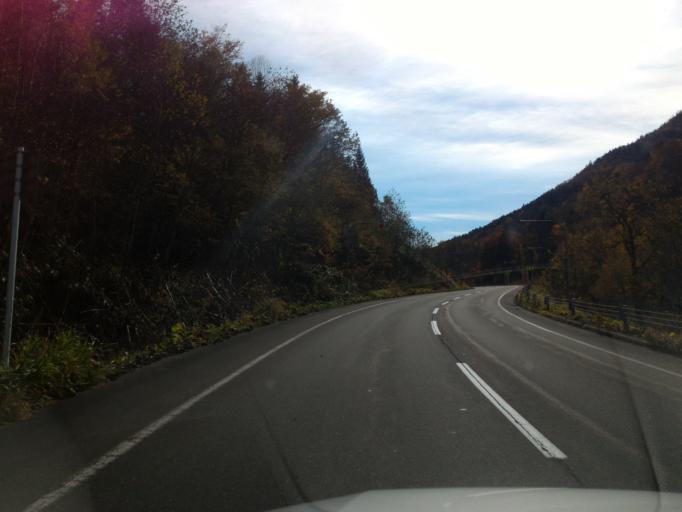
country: JP
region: Hokkaido
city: Shimo-furano
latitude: 43.3602
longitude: 142.2425
